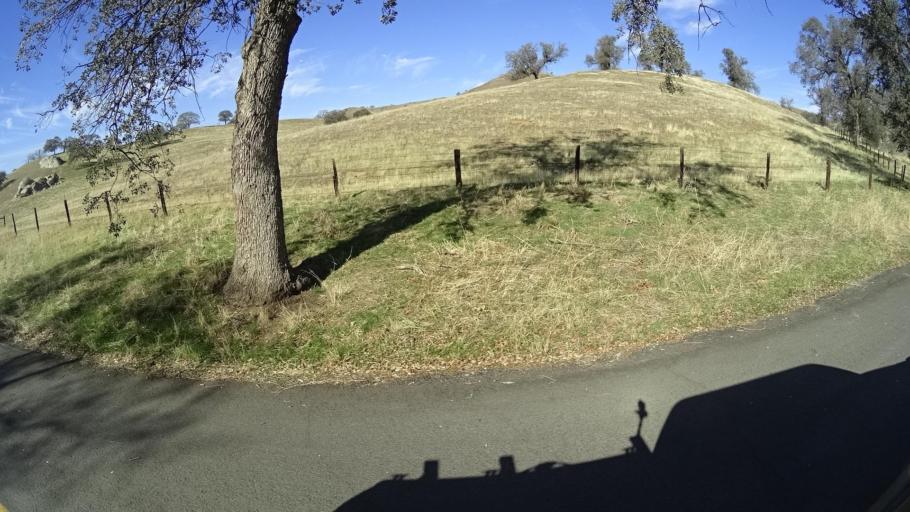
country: US
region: California
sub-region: Tulare County
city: Richgrove
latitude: 35.6778
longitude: -118.8464
